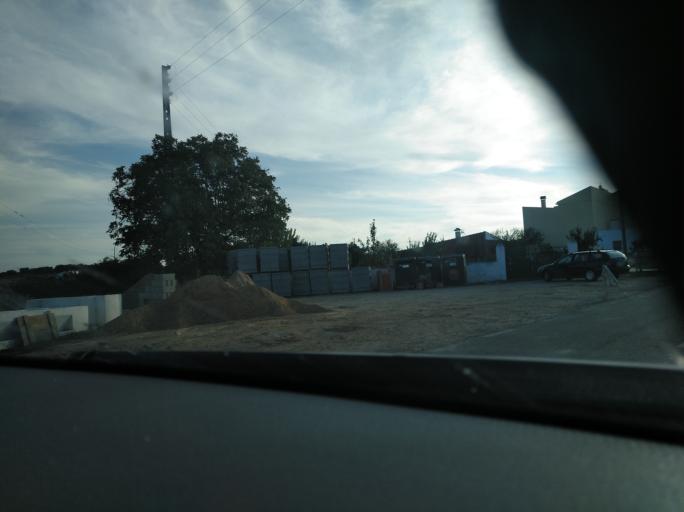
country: PT
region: Portalegre
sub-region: Fronteira
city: Fronteira
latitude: 38.9557
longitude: -7.6663
